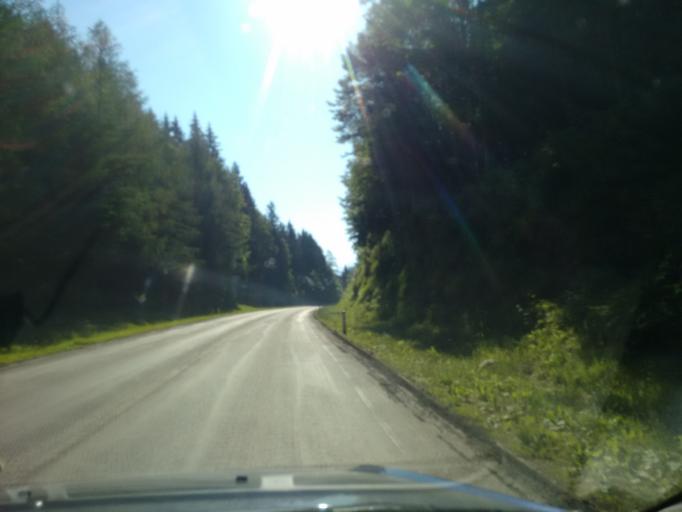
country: AT
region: Styria
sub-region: Politischer Bezirk Liezen
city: Altaussee
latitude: 47.6248
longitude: 13.7466
